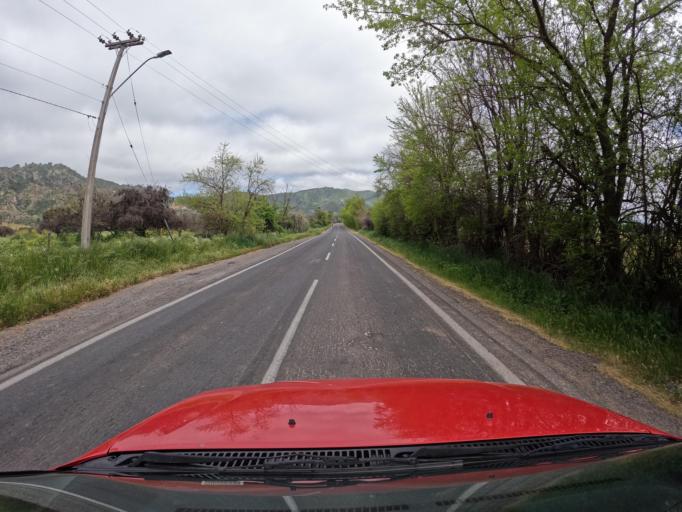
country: CL
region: O'Higgins
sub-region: Provincia de Colchagua
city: Santa Cruz
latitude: -34.6592
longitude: -71.4047
